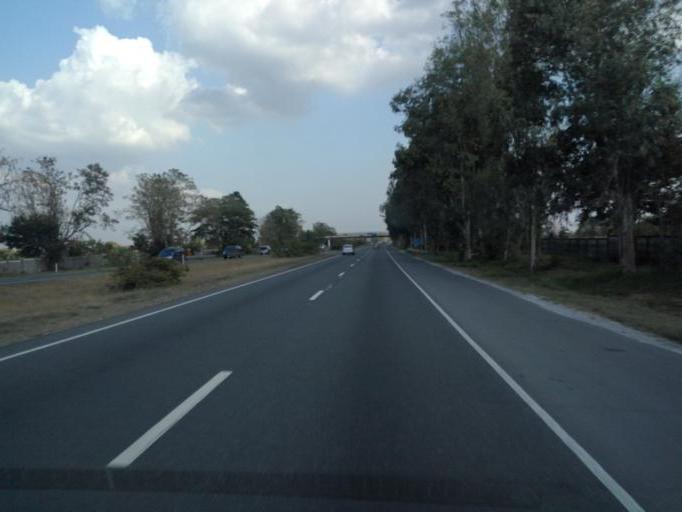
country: PH
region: Central Luzon
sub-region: Province of Pampanga
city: Acli
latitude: 15.1244
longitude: 120.6490
